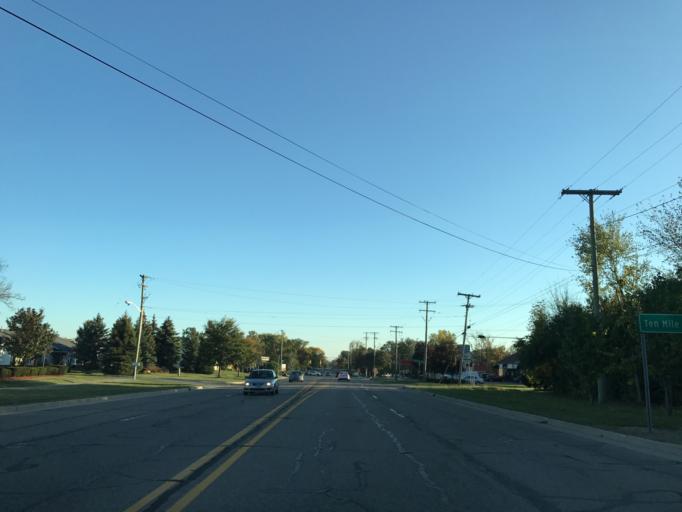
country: US
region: Michigan
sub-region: Oakland County
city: Farmington
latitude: 42.4730
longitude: -83.3379
